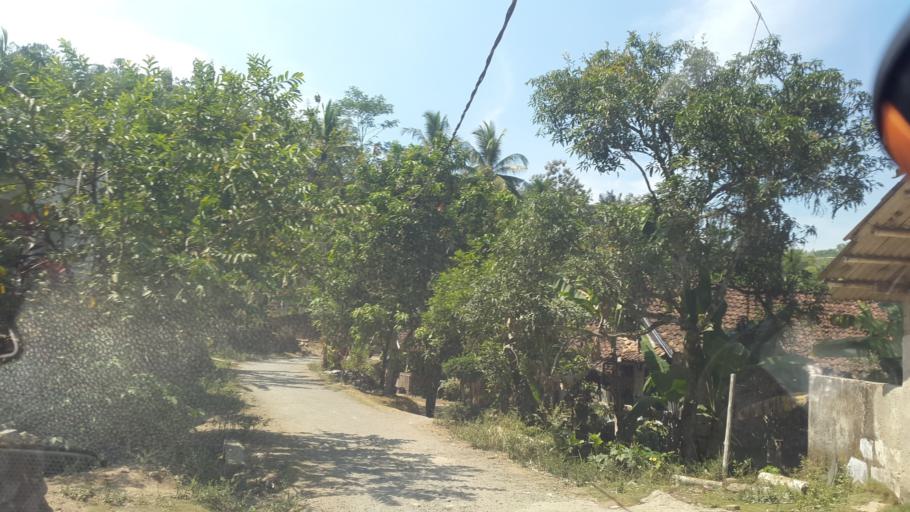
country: ID
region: West Java
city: Bojonggaling
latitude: -6.9402
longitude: 106.6119
